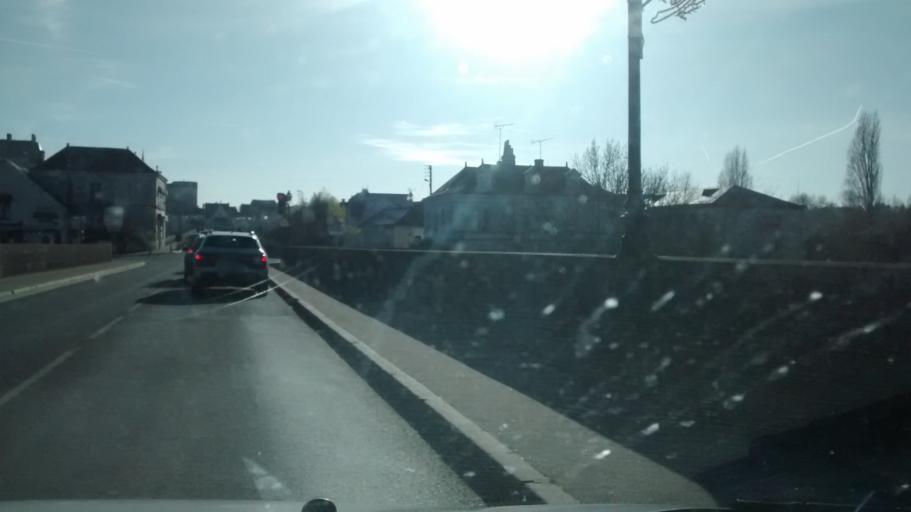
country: FR
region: Centre
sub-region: Departement d'Indre-et-Loire
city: Amboise
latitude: 47.4165
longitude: 0.9822
